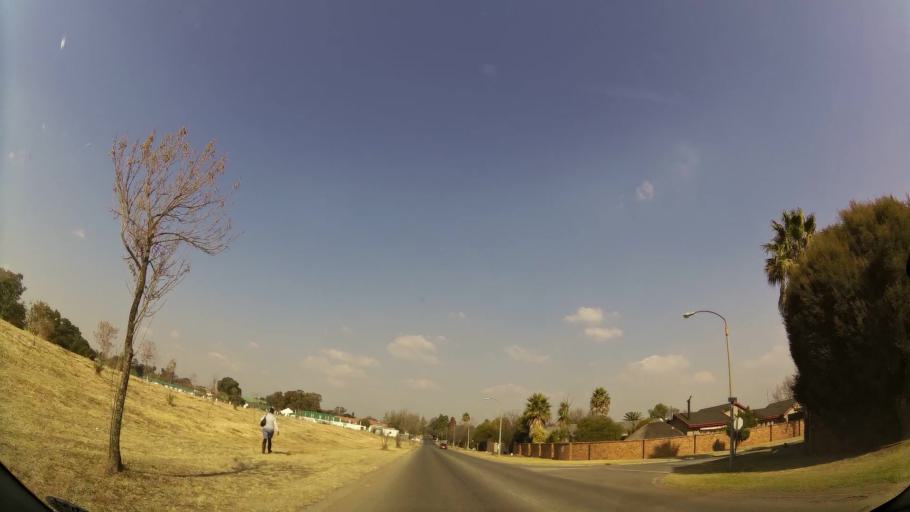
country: ZA
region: Gauteng
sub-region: Ekurhuleni Metropolitan Municipality
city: Benoni
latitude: -26.1454
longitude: 28.2890
